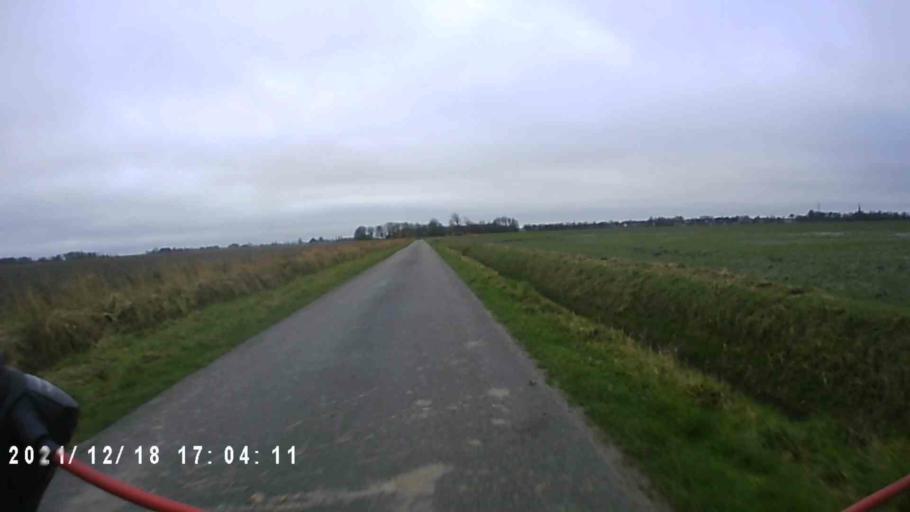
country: NL
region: Friesland
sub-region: Gemeente Dongeradeel
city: Holwerd
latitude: 53.3713
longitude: 5.9220
